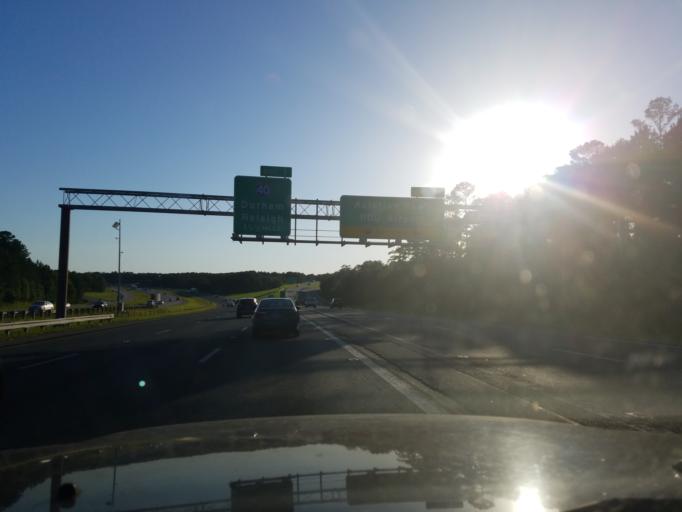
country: US
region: North Carolina
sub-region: Wake County
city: Morrisville
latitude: 35.8947
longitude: -78.8056
